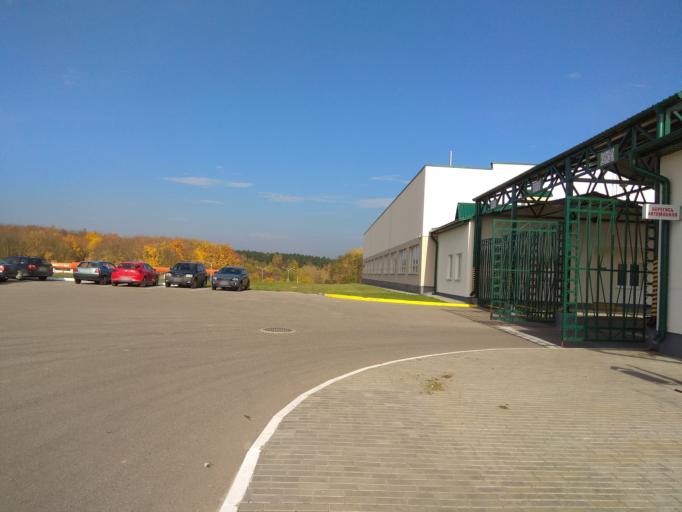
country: BY
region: Grodnenskaya
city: Hrodna
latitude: 53.7104
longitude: 23.7978
